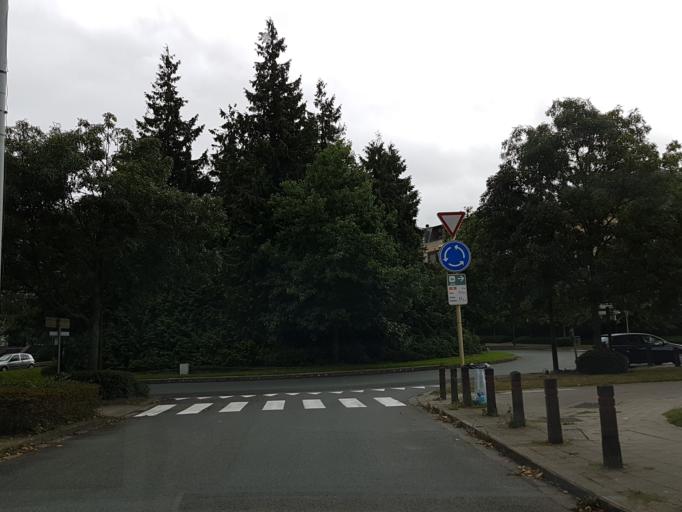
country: BE
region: Flanders
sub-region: Provincie Vlaams-Brabant
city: Kraainem
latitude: 50.8555
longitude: 4.4401
